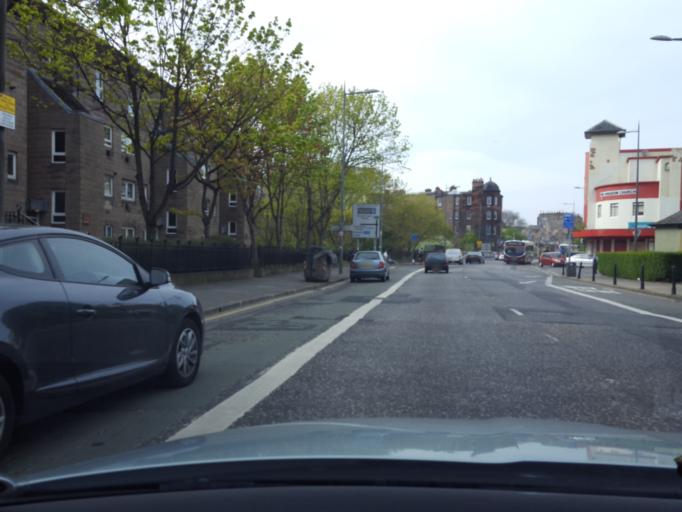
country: GB
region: Scotland
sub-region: West Lothian
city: Seafield
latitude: 55.9741
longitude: -3.1774
